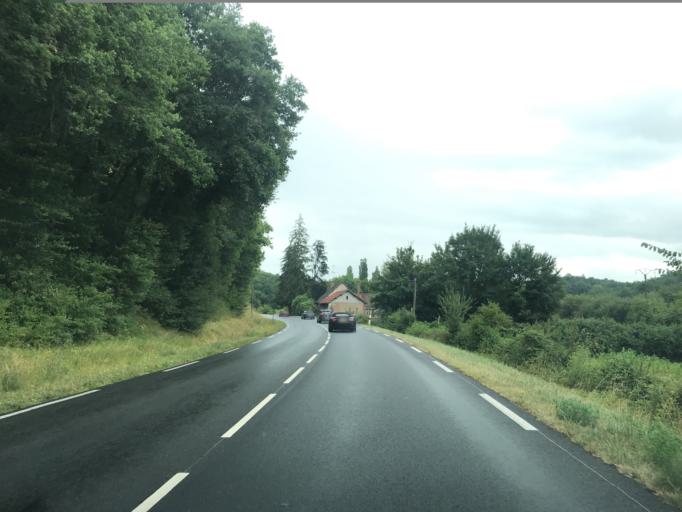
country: FR
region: Aquitaine
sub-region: Departement de la Dordogne
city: Boulazac
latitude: 45.1113
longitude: 0.8325
